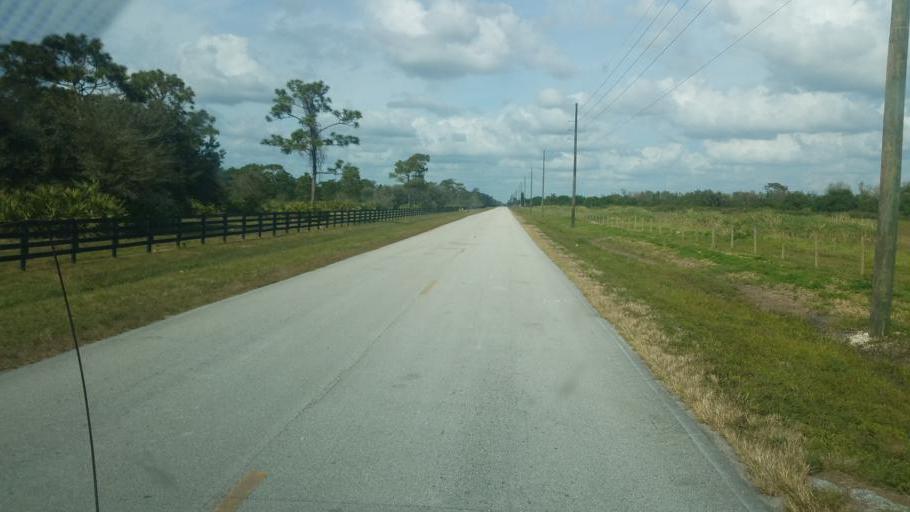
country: US
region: Florida
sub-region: Okeechobee County
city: Cypress Quarters
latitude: 27.4732
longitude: -80.7712
